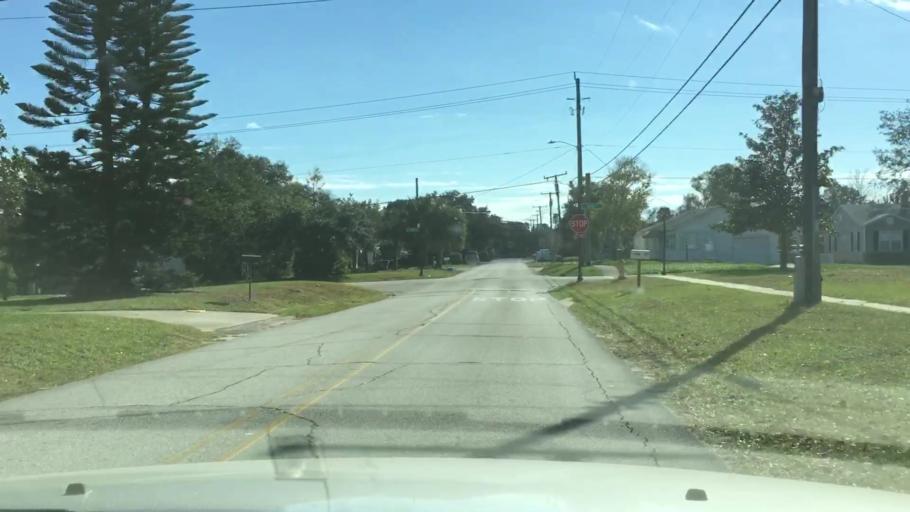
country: US
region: Florida
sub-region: Volusia County
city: Holly Hill
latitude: 29.2303
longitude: -81.0308
